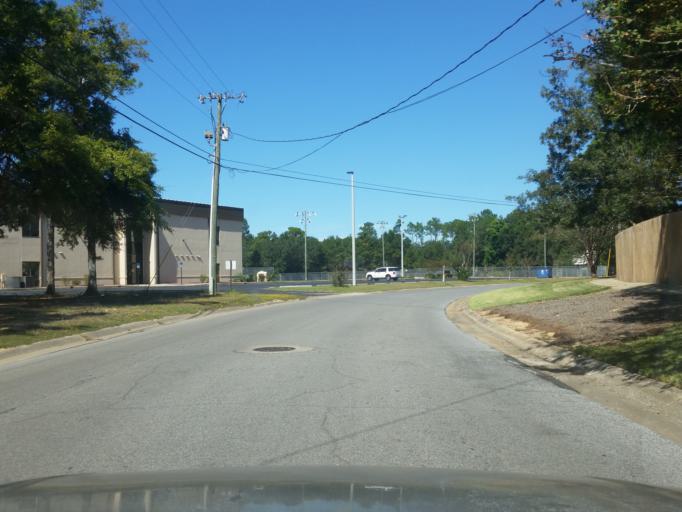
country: US
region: Florida
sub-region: Escambia County
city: East Pensacola Heights
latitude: 30.4608
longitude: -87.1773
